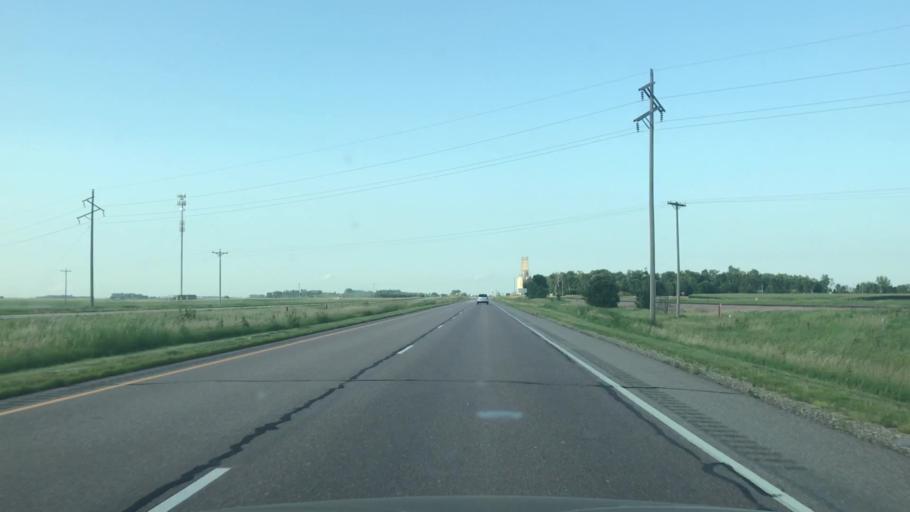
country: US
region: Minnesota
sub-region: Jackson County
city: Lakefield
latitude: 43.7602
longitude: -95.3765
